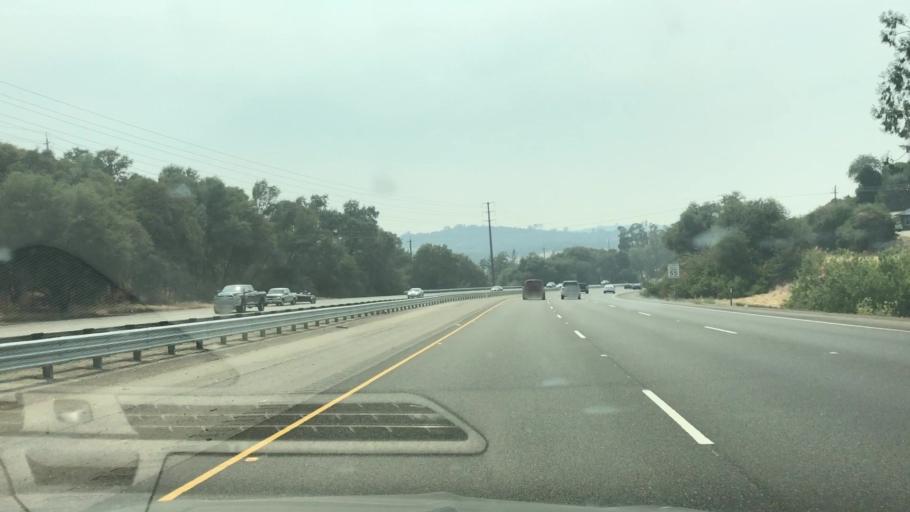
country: US
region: California
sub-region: El Dorado County
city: Cameron Park
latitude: 38.6579
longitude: -120.9836
